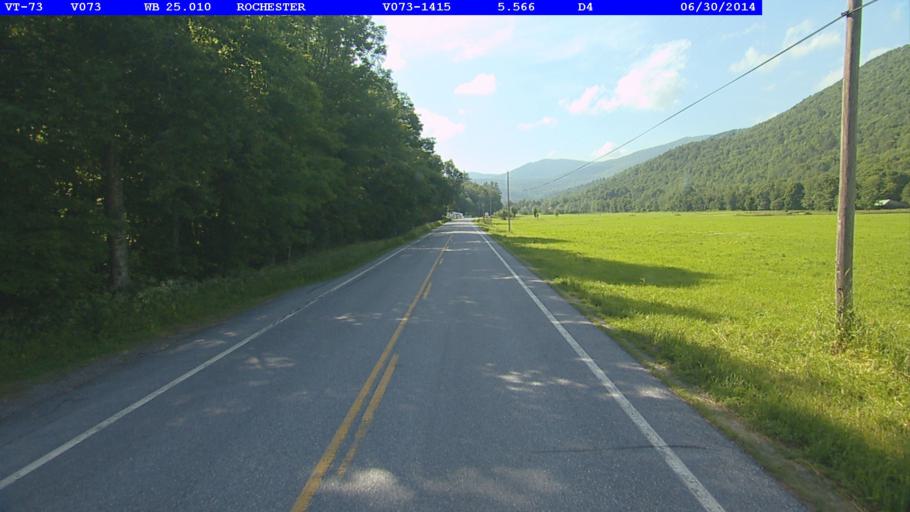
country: US
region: Vermont
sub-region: Orange County
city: Randolph
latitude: 43.8526
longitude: -72.8631
